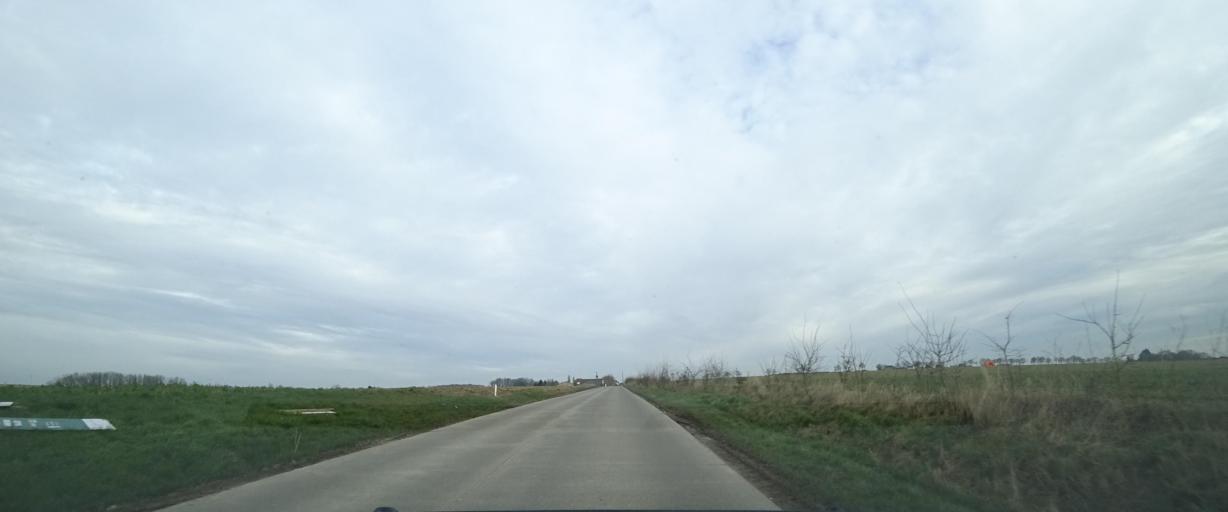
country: BE
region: Wallonia
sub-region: Province de Namur
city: Sombreffe
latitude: 50.5101
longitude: 4.6560
